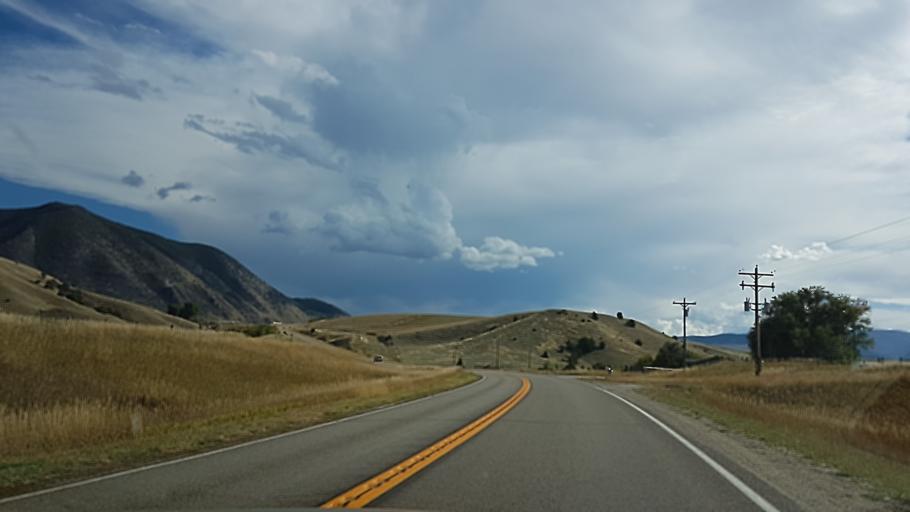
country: US
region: Montana
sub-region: Jefferson County
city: Whitehall
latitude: 45.8385
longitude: -111.9403
